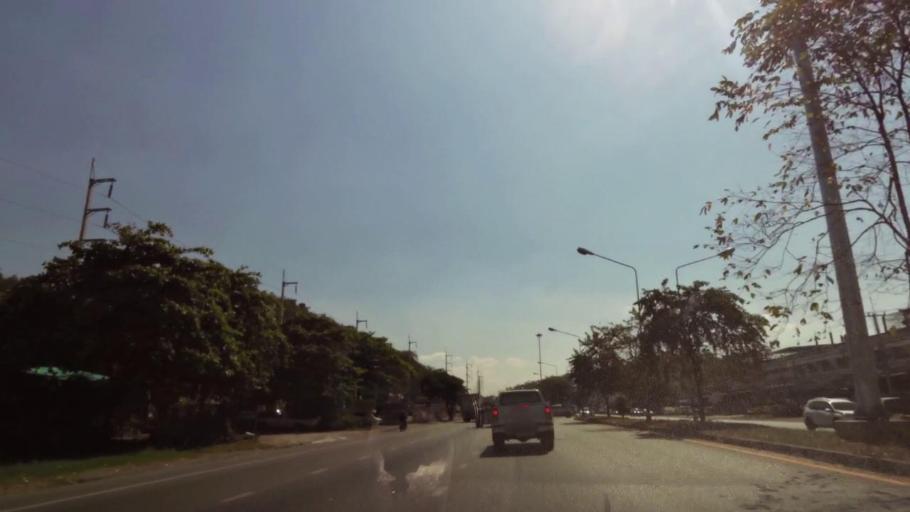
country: TH
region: Nakhon Sawan
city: Nakhon Sawan
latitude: 15.7176
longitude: 100.1178
